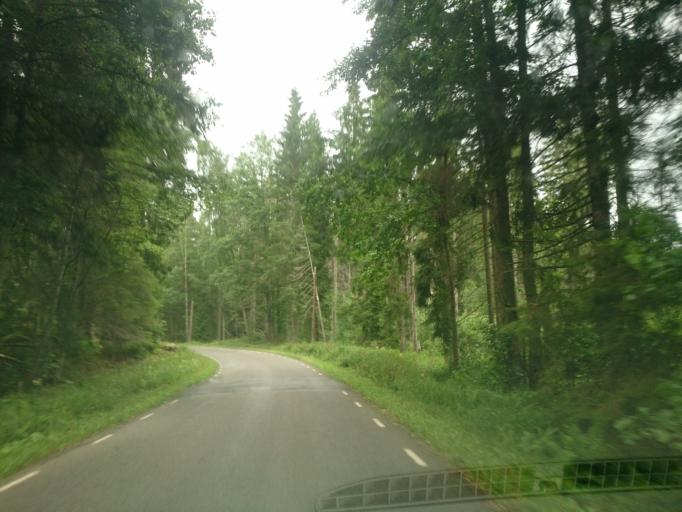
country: SE
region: OEstergoetland
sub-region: Atvidabergs Kommun
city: Atvidaberg
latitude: 58.2893
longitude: 16.0956
